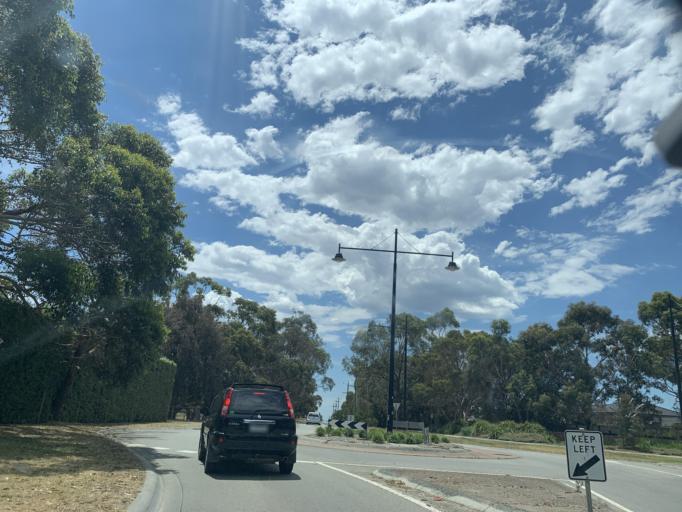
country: AU
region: Victoria
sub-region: Casey
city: Cranbourne South
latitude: -38.1453
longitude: 145.2460
